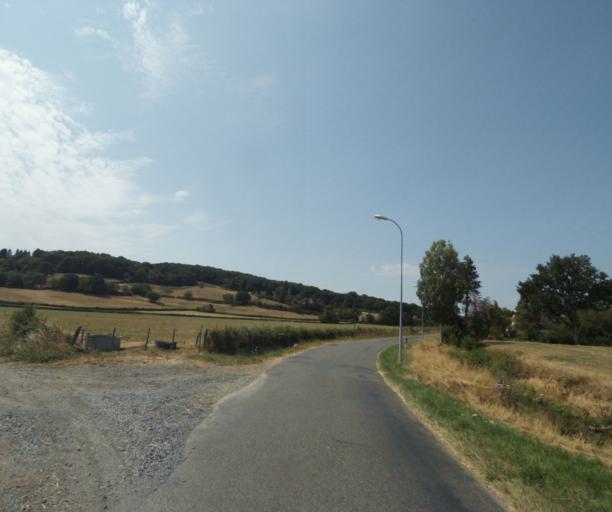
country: FR
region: Bourgogne
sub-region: Departement de Saone-et-Loire
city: Gueugnon
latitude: 46.6083
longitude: 4.0441
